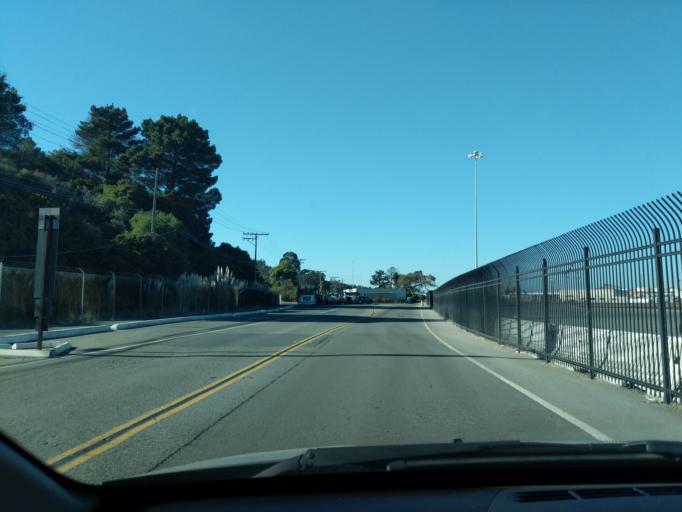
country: US
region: California
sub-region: Contra Costa County
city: Richmond
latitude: 37.9116
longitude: -122.3679
